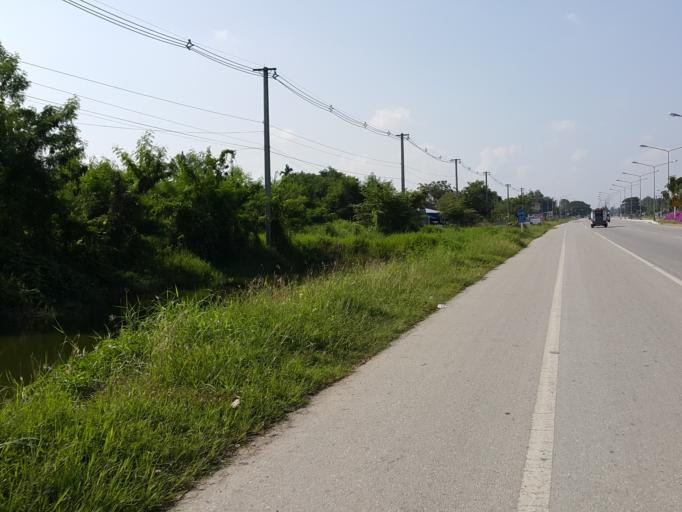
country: TH
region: Chiang Mai
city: San Kamphaeng
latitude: 18.7582
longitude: 99.0769
